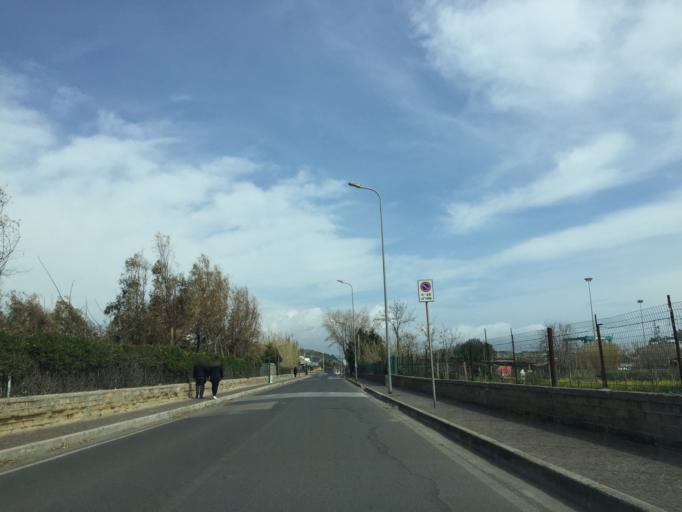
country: IT
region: Campania
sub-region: Provincia di Napoli
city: Bacoli
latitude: 40.7888
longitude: 14.0757
